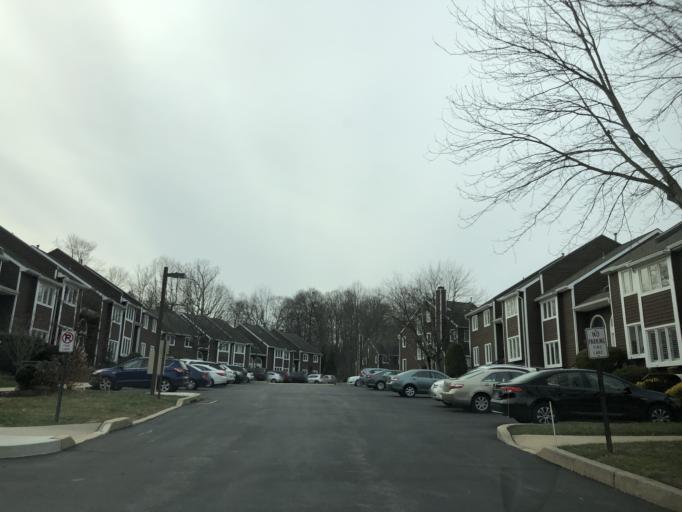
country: US
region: Pennsylvania
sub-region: Chester County
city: Exton
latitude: 40.0355
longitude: -75.6396
